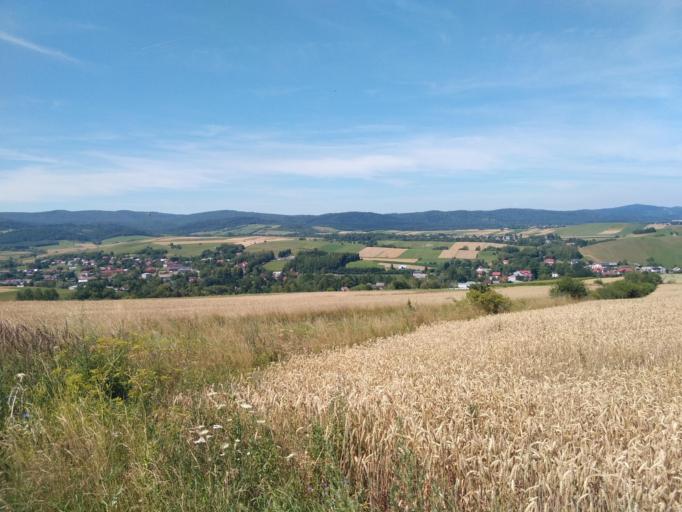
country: PL
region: Subcarpathian Voivodeship
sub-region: Powiat sanocki
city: Bukowsko
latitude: 49.5135
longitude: 22.0449
